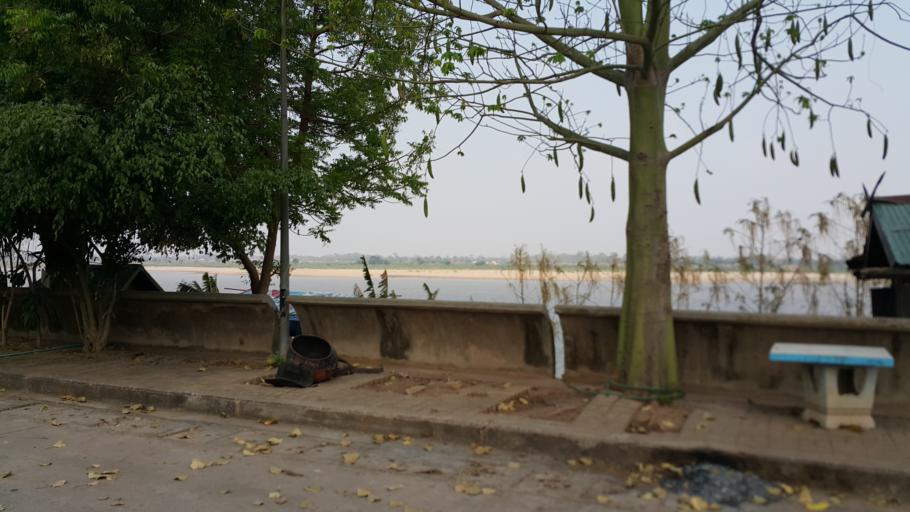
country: TH
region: Nakhon Phanom
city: That Phanom
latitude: 16.9411
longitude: 104.7292
